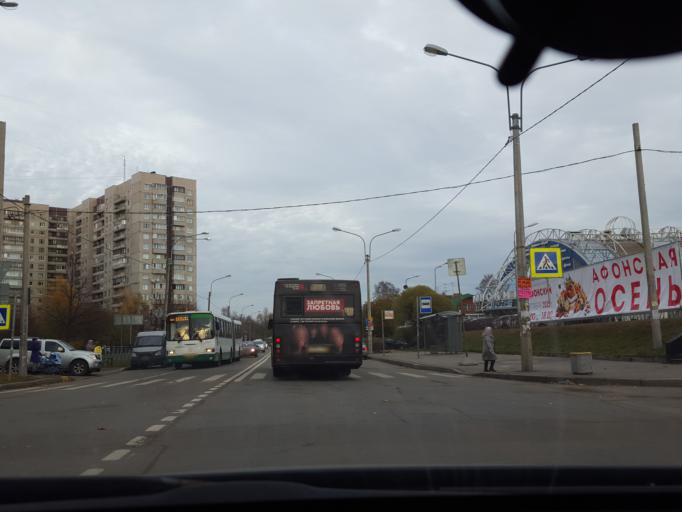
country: RU
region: St.-Petersburg
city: Kolomyagi
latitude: 60.0254
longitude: 30.3017
